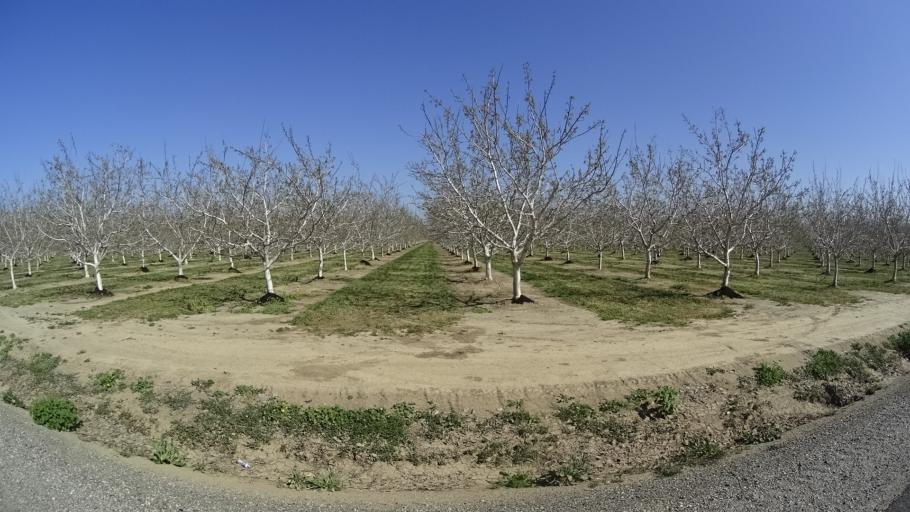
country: US
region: California
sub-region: Glenn County
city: Hamilton City
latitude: 39.6597
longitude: -122.0395
